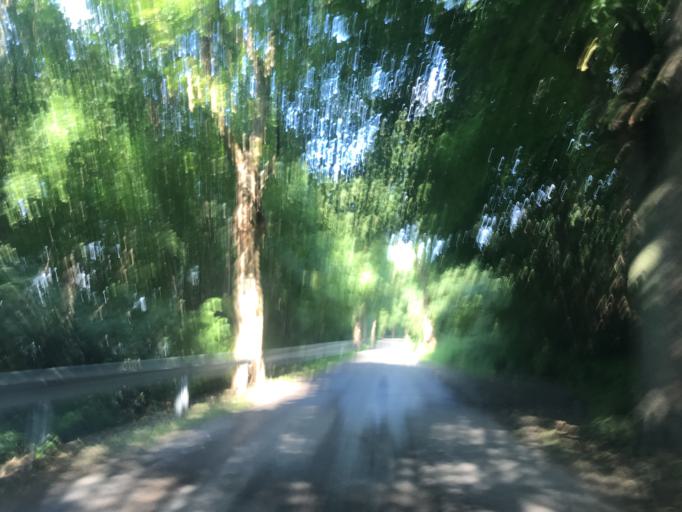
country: PL
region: Kujawsko-Pomorskie
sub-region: Powiat brodnicki
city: Brzozie
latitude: 53.3050
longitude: 19.6130
